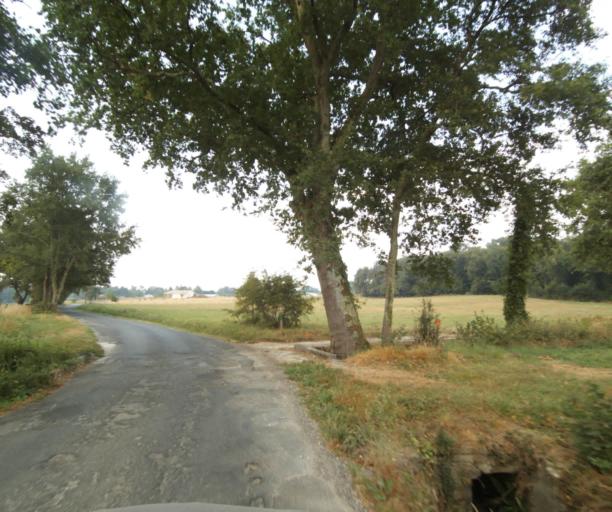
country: FR
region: Aquitaine
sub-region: Departement de la Gironde
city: La Sauve
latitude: 44.7804
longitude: -0.3214
